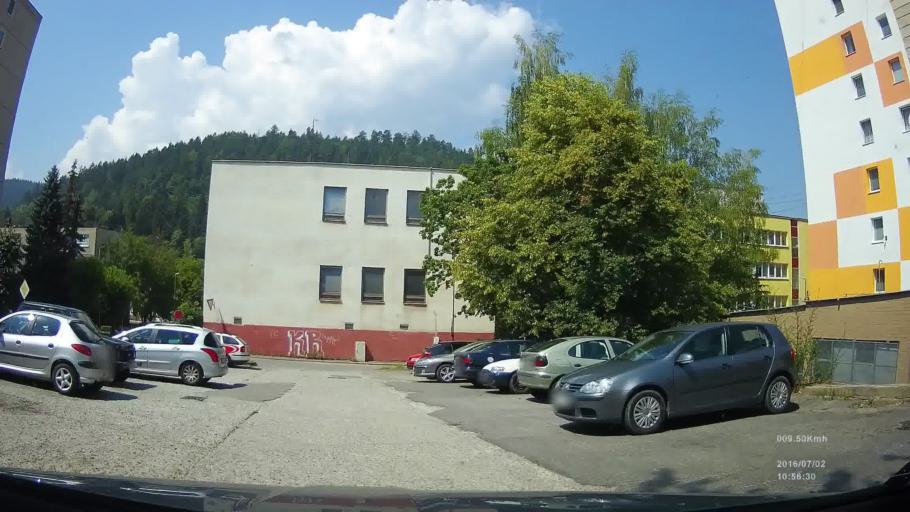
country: SK
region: Kosicky
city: Krompachy
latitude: 48.9150
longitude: 20.8750
